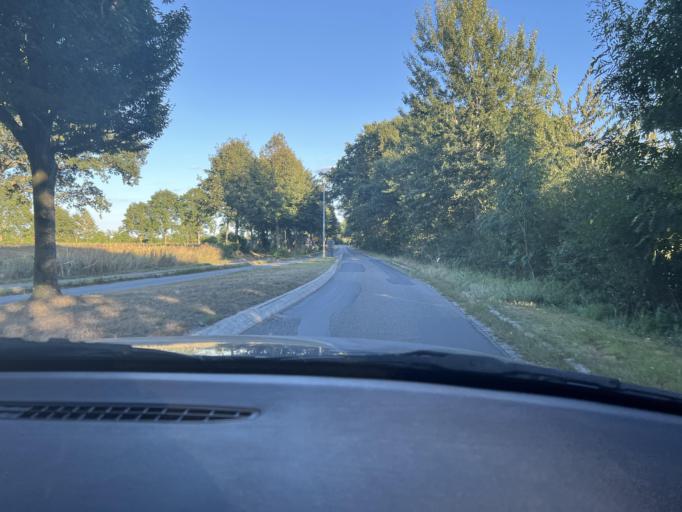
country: DE
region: Schleswig-Holstein
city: Kleve
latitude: 54.2938
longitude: 9.1309
